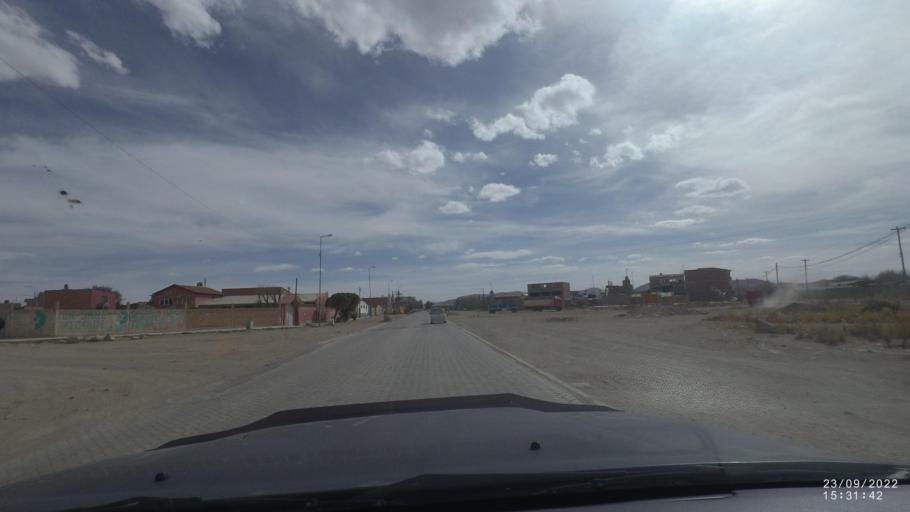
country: BO
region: Oruro
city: Oruro
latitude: -17.9744
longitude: -67.0547
